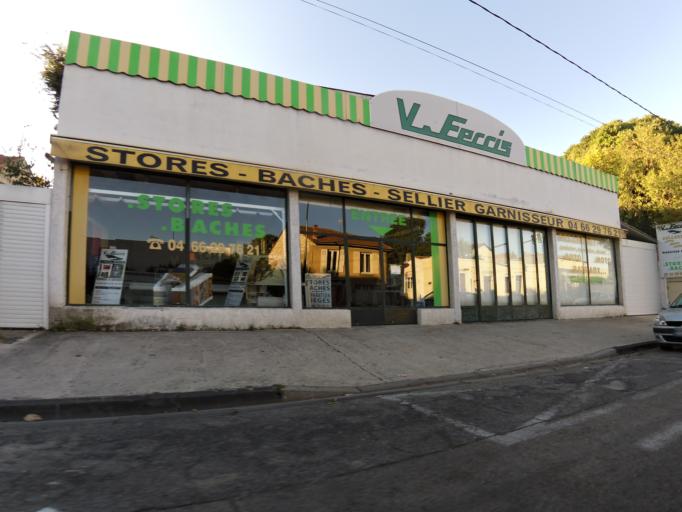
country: FR
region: Languedoc-Roussillon
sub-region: Departement du Gard
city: Nimes
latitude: 43.8222
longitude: 4.3498
